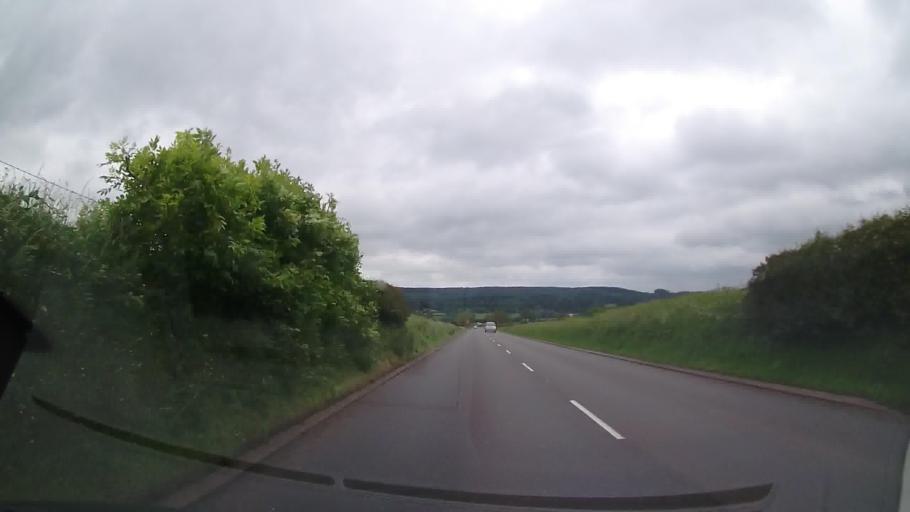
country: GB
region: England
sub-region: Staffordshire
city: Standon
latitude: 52.9371
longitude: -2.3557
